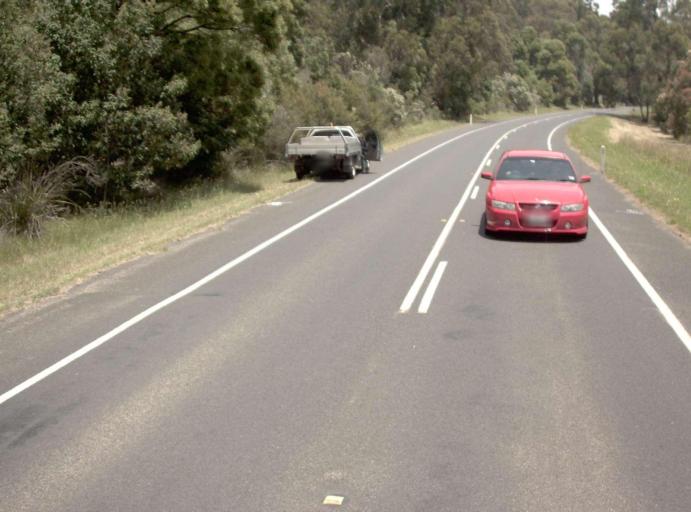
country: AU
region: Victoria
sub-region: Latrobe
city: Traralgon
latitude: -38.3594
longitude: 146.7450
